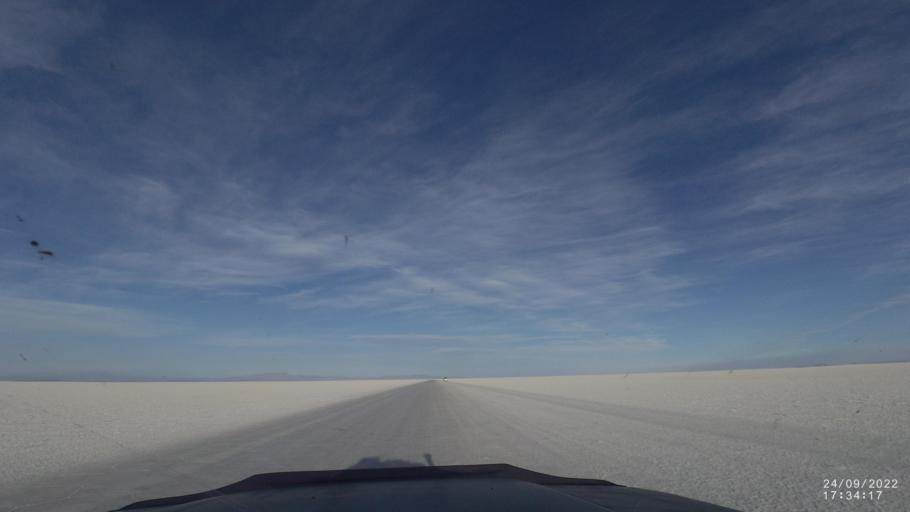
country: BO
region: Potosi
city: Colchani
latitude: -20.3206
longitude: -67.2856
